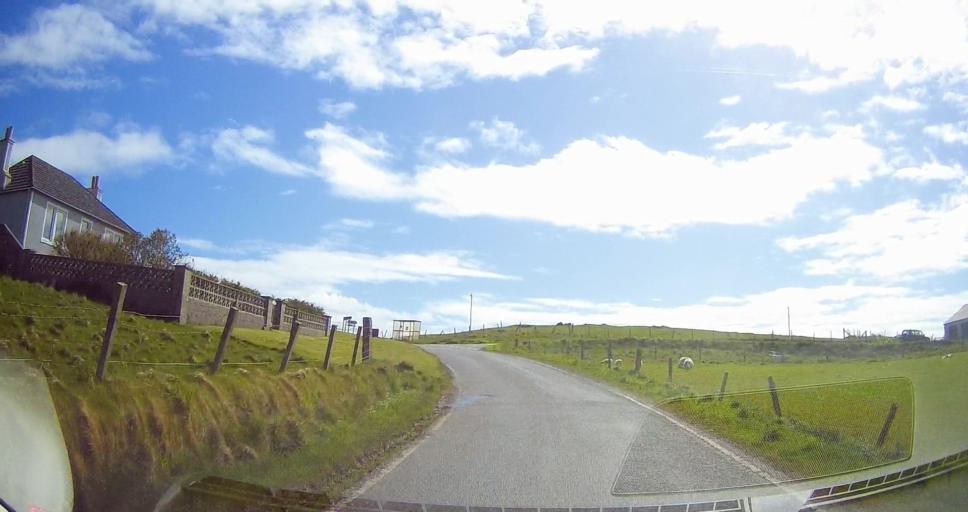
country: GB
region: Scotland
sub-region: Shetland Islands
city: Sandwick
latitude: 59.9399
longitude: -1.3229
